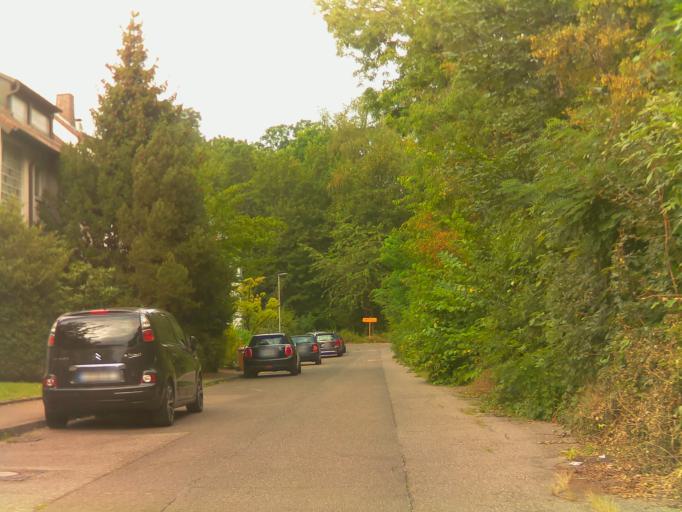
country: DE
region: Baden-Wuerttemberg
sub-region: Regierungsbezirk Stuttgart
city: Leinfelden-Echterdingen
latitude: 48.7402
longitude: 9.1454
